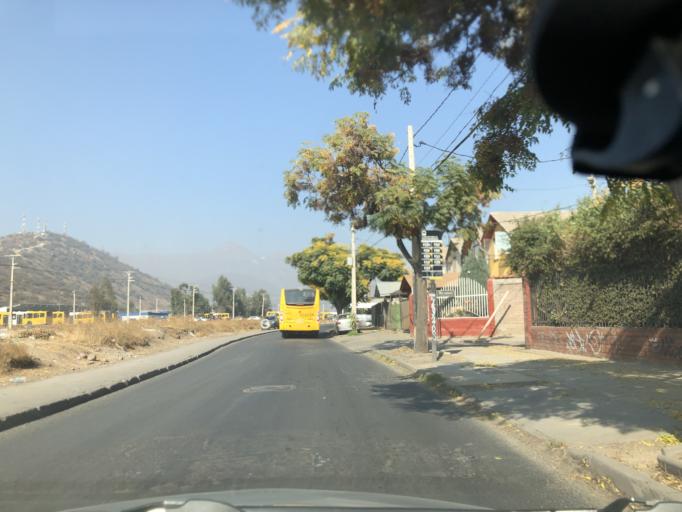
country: CL
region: Santiago Metropolitan
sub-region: Provincia de Cordillera
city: Puente Alto
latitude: -33.6021
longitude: -70.5560
